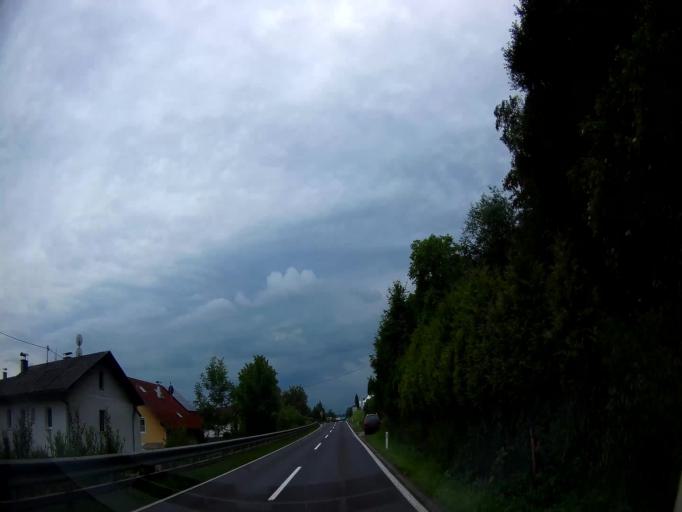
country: AT
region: Upper Austria
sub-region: Politischer Bezirk Braunau am Inn
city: Braunau am Inn
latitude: 48.1613
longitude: 13.1172
